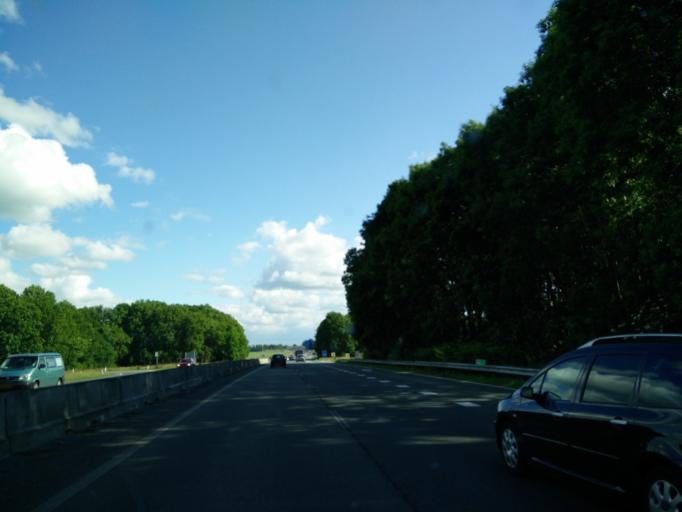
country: NL
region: Groningen
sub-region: Gemeente Haren
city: Haren
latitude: 53.1262
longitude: 6.6101
